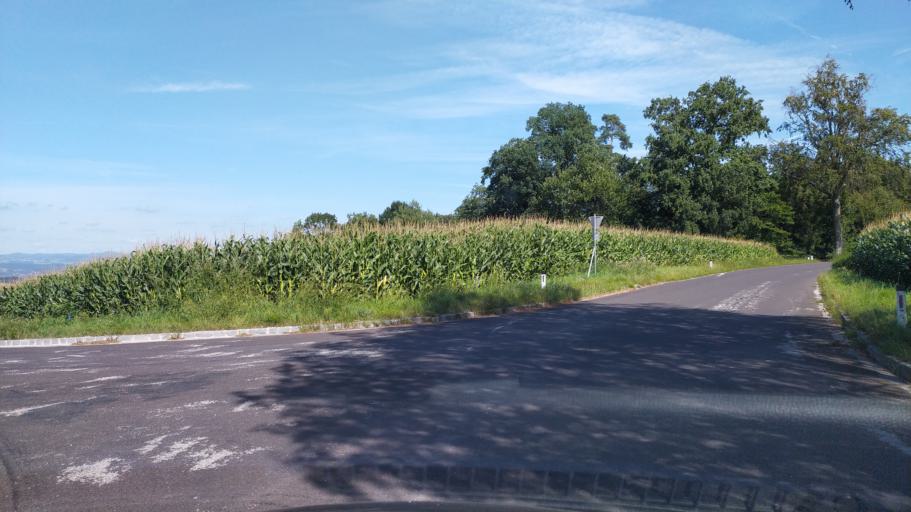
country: AT
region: Lower Austria
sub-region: Politischer Bezirk Amstetten
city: Strengberg
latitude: 48.1198
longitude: 14.6458
